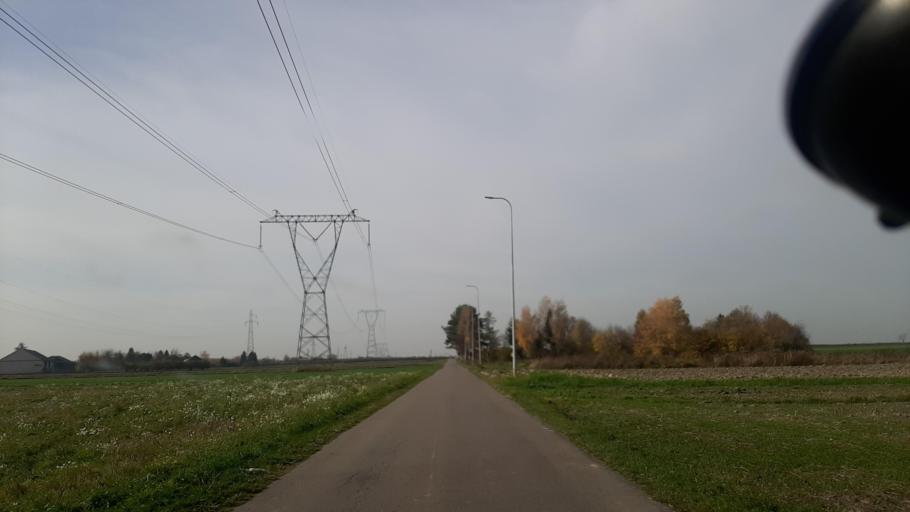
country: PL
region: Lublin Voivodeship
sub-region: Powiat lubelski
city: Lublin
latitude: 51.3331
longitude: 22.5388
